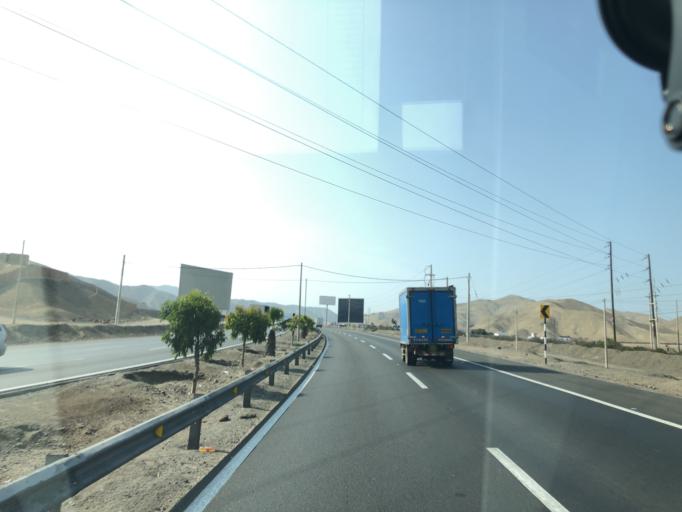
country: PE
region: Lima
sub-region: Lima
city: San Bartolo
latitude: -12.4090
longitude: -76.7566
